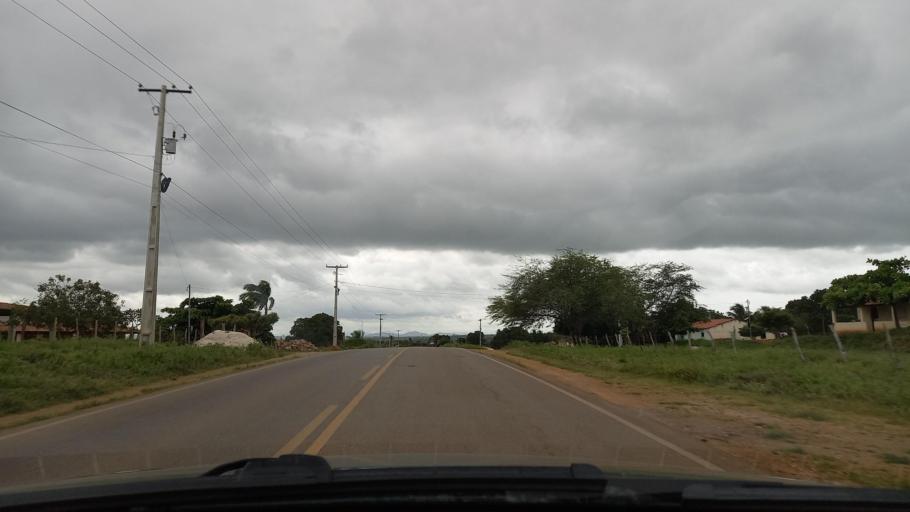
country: BR
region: Sergipe
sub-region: Caninde De Sao Francisco
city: Caninde de Sao Francisco
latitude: -9.6807
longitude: -37.8078
